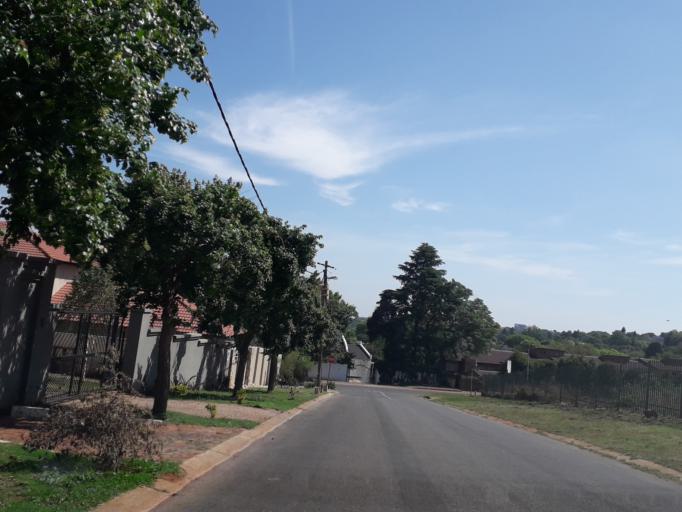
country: ZA
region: Gauteng
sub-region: City of Johannesburg Metropolitan Municipality
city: Johannesburg
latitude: -26.1184
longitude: 27.9923
